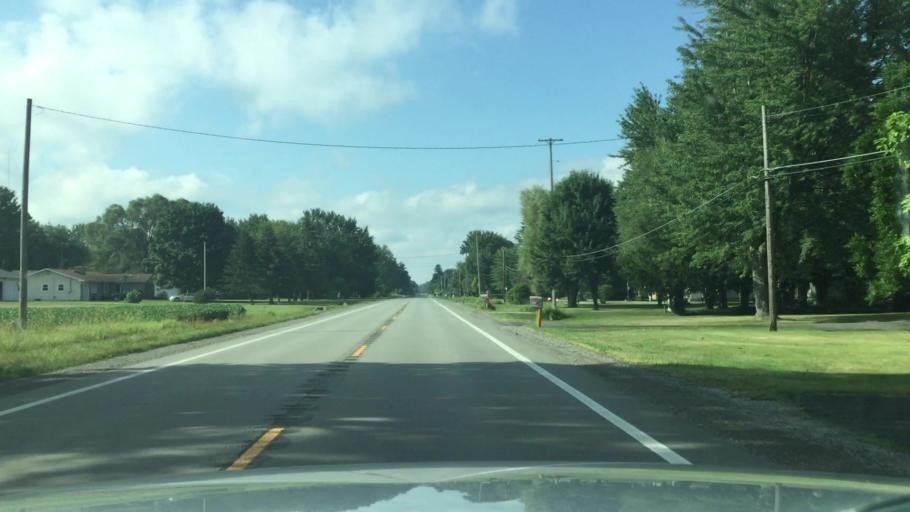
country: US
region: Michigan
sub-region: Saginaw County
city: Birch Run
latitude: 43.2404
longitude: -83.7354
